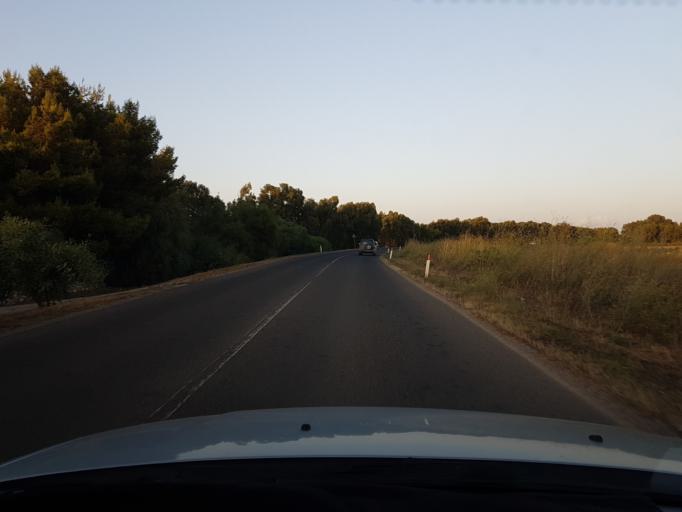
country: IT
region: Sardinia
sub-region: Provincia di Oristano
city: Cabras
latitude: 39.9180
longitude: 8.4930
